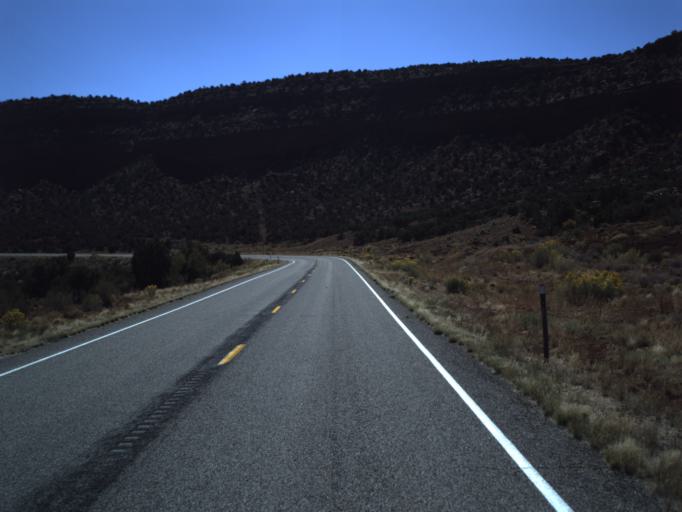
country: US
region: Utah
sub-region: San Juan County
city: Blanding
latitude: 37.6065
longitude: -110.0794
